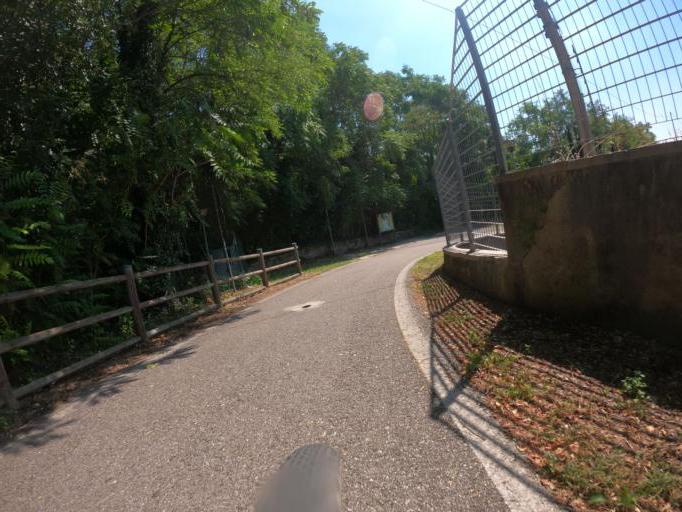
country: IT
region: Veneto
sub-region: Provincia di Verona
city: Volargne
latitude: 45.5548
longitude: 10.8242
